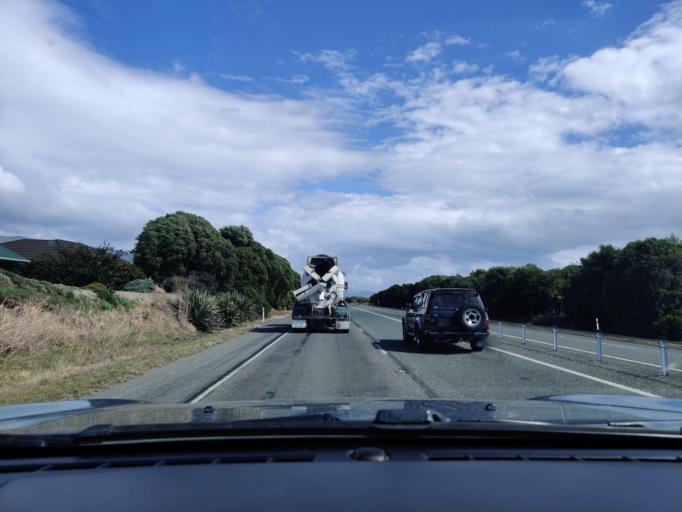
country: NZ
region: Tasman
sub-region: Tasman District
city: Richmond
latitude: -41.3095
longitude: 173.2193
